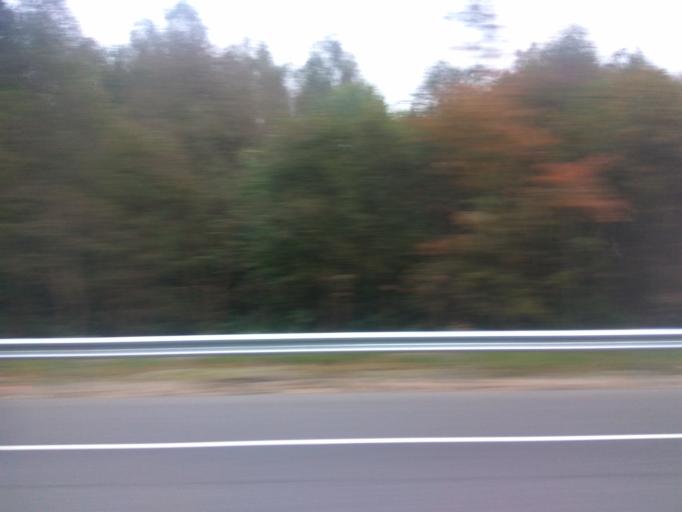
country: RU
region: Moskovskaya
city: Krasnoarmeysk
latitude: 56.0293
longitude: 38.1835
